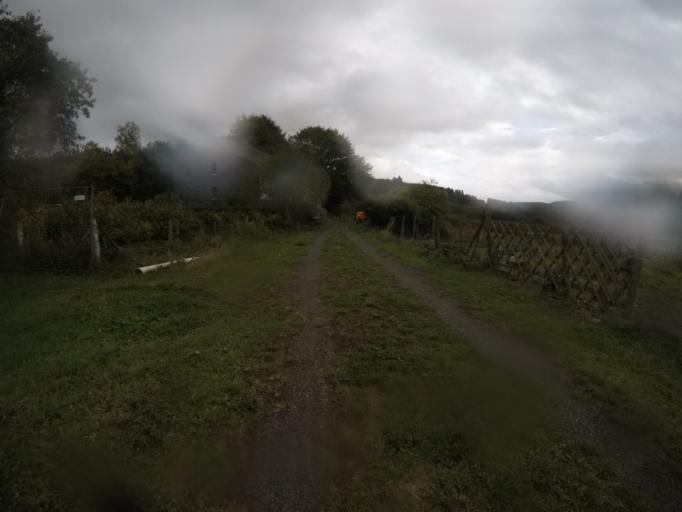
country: BE
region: Wallonia
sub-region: Province du Luxembourg
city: Fauvillers
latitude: 49.8747
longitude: 5.6836
